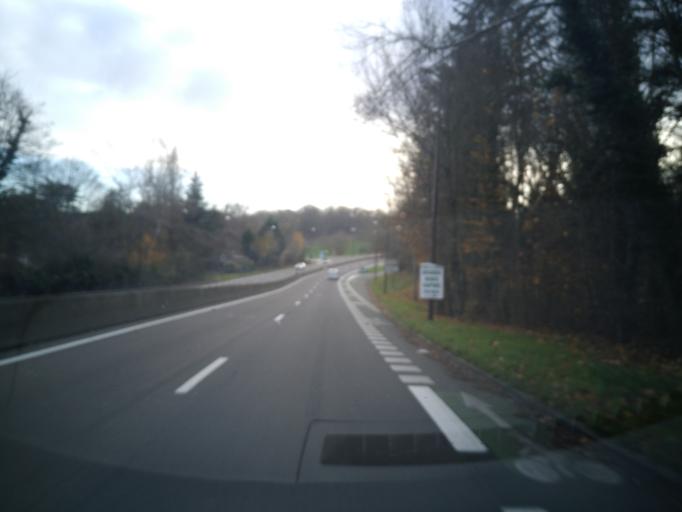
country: FR
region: Ile-de-France
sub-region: Departement des Yvelines
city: Guyancourt
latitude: 48.7802
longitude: 2.0958
